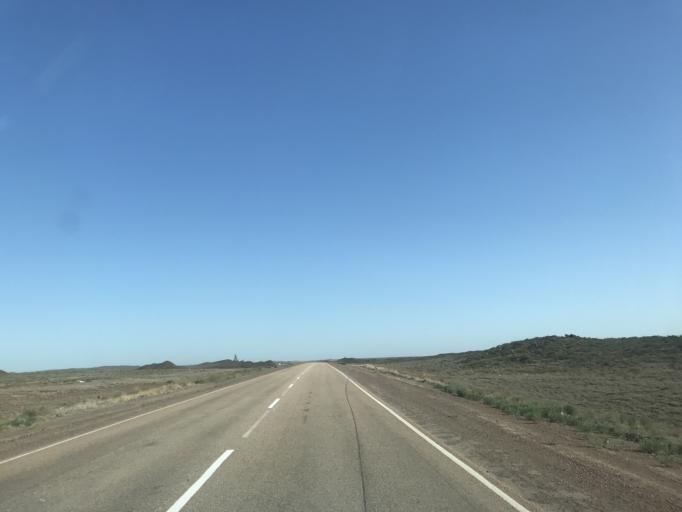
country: KZ
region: Zhambyl
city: Mynaral
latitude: 45.4243
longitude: 73.6212
